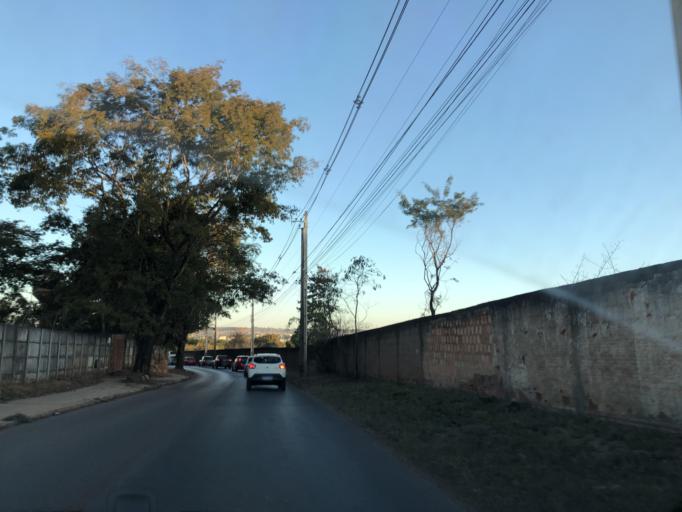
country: BR
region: Federal District
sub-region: Brasilia
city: Brasilia
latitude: -15.8767
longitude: -47.7804
